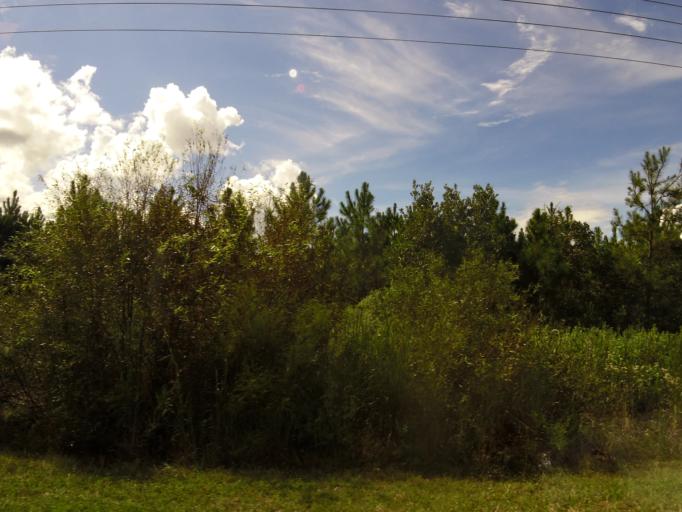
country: US
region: Florida
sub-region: Union County
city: Lake Butler
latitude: 30.0082
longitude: -82.3147
